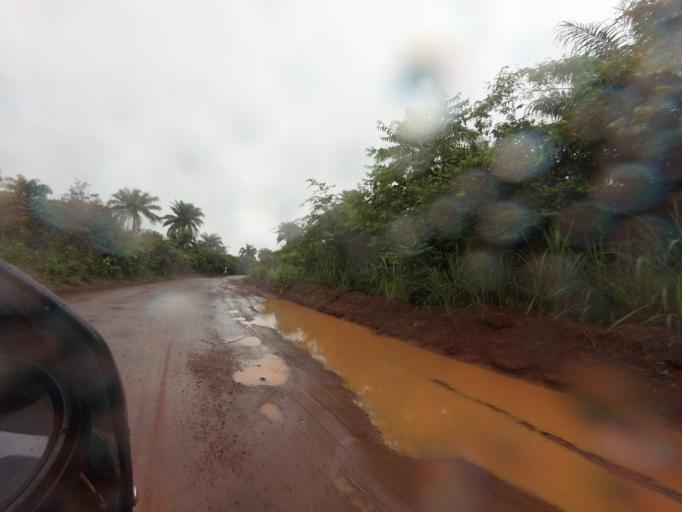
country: SL
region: Northern Province
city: Kambia
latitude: 9.1756
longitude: -12.8789
